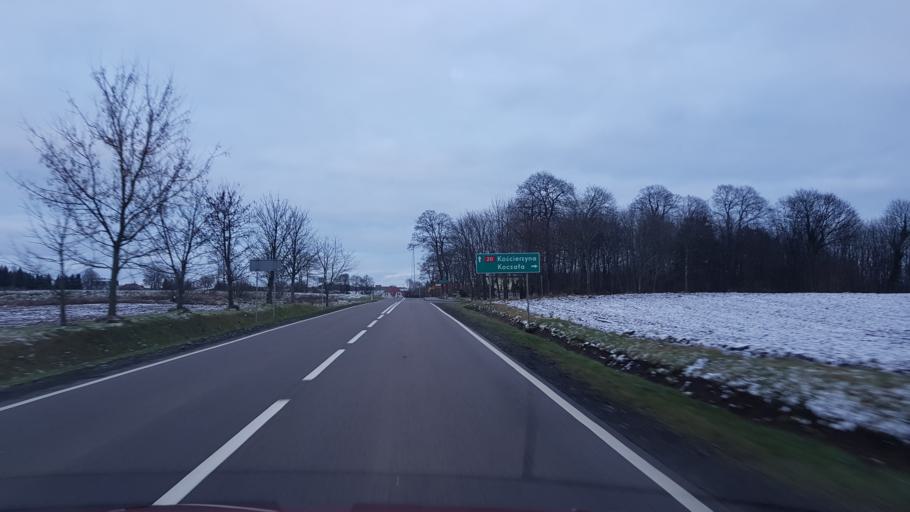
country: PL
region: Pomeranian Voivodeship
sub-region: Powiat czluchowski
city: Koczala
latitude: 54.0207
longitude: 17.1631
